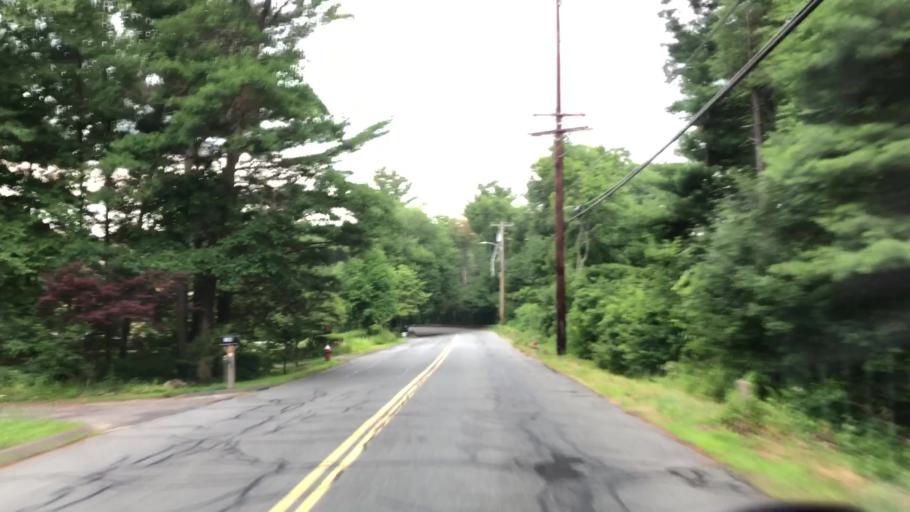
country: US
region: Massachusetts
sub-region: Hampden County
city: Holyoke
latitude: 42.1907
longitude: -72.6714
